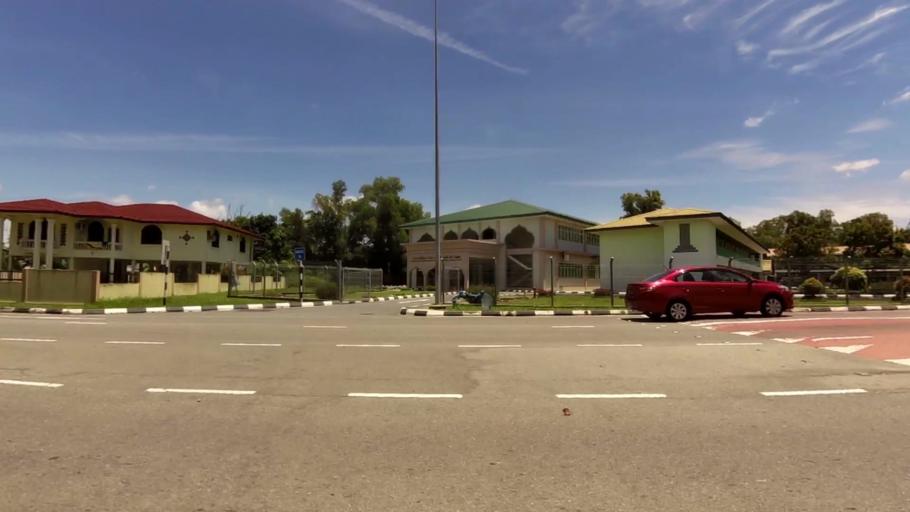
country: BN
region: Brunei and Muara
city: Bandar Seri Begawan
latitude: 4.9346
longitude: 114.9384
